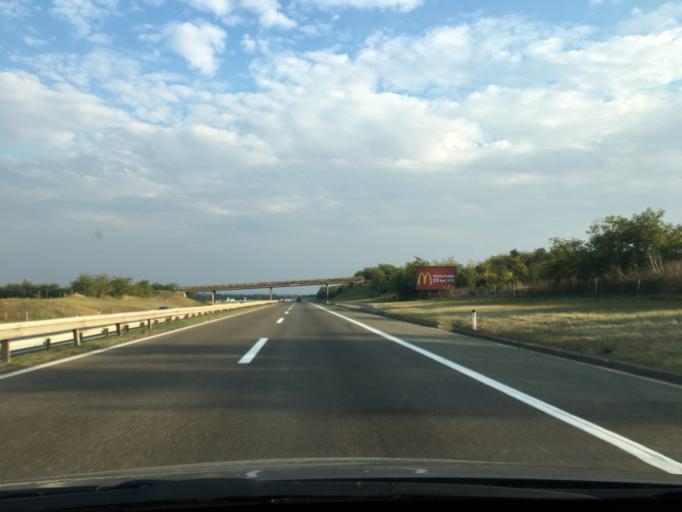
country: RS
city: Lugavcina
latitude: 44.4862
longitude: 21.0275
